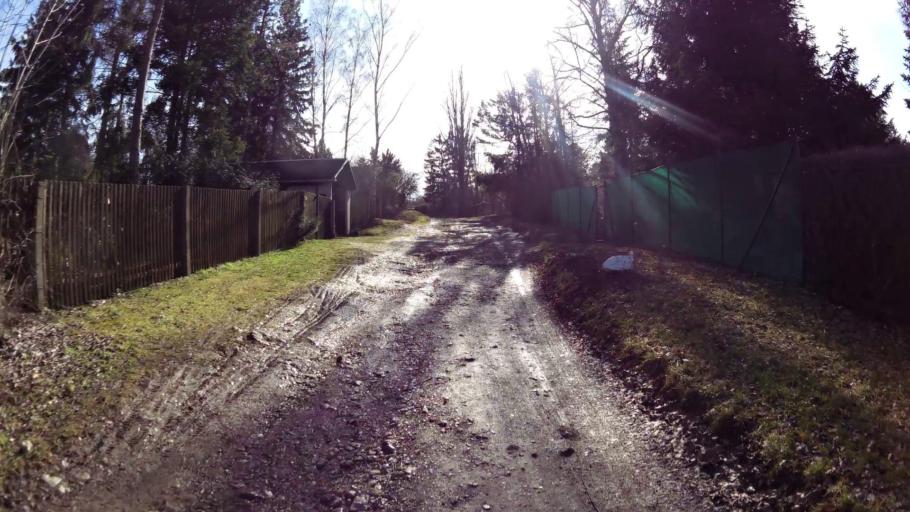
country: DE
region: Thuringia
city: Weimar
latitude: 50.9606
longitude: 11.3284
